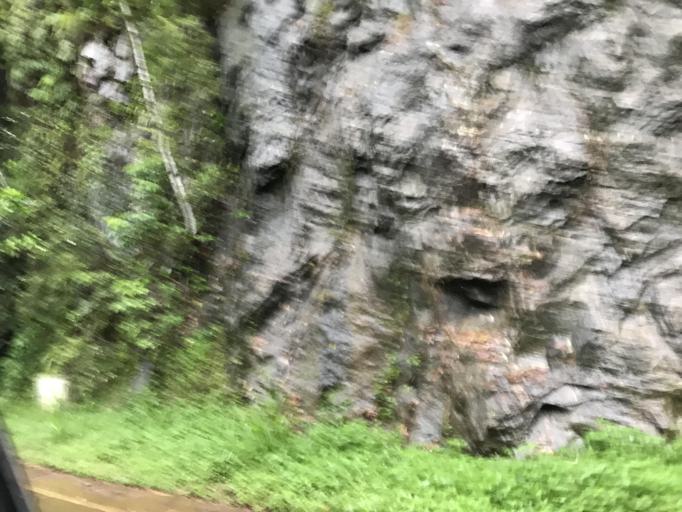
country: LK
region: Sabaragamuwa
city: Ratnapura
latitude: 6.5393
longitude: 80.3051
